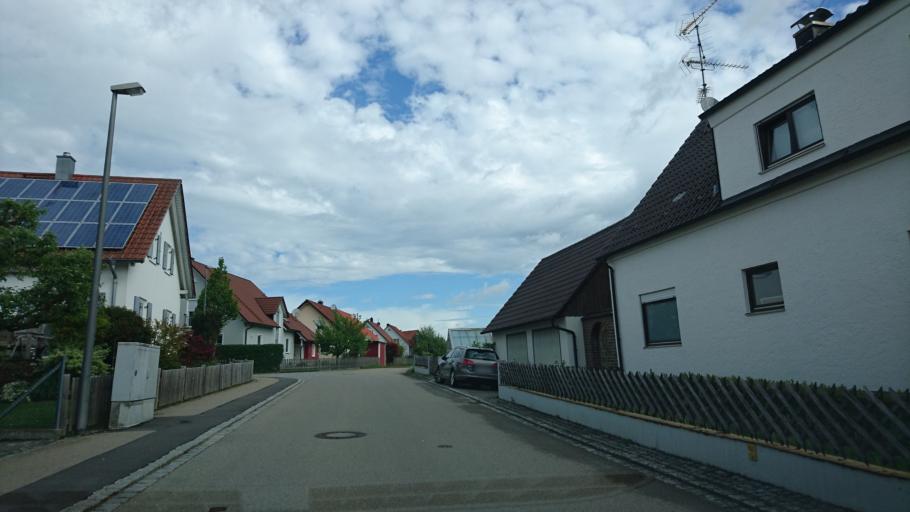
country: DE
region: Bavaria
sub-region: Swabia
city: Zusmarshausen
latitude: 48.4185
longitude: 10.5885
